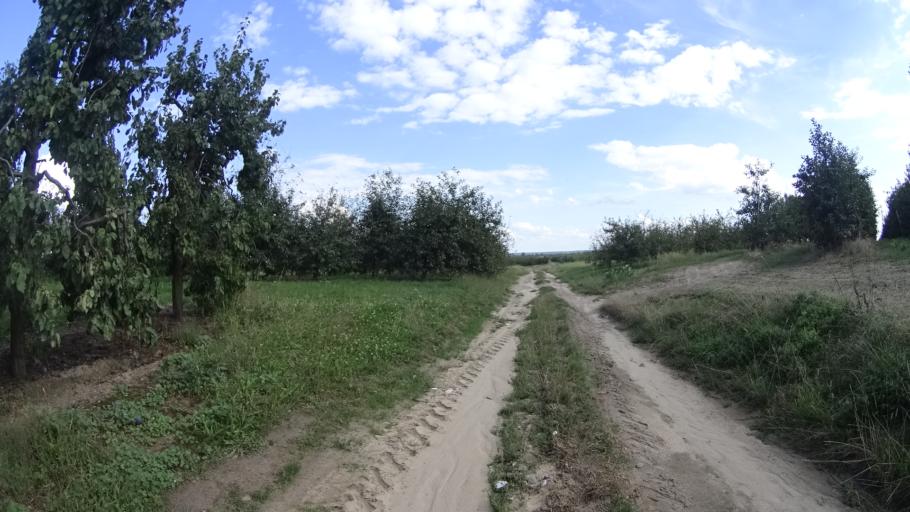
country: PL
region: Masovian Voivodeship
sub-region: Powiat bialobrzeski
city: Wysmierzyce
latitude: 51.6679
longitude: 20.8093
